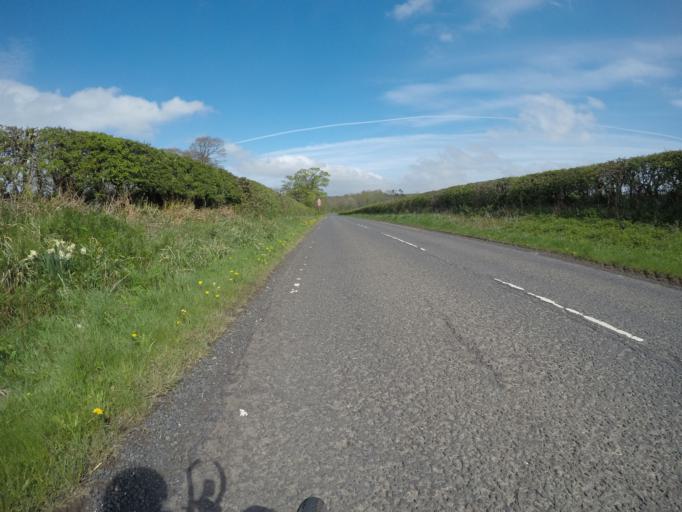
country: GB
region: Scotland
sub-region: East Ayrshire
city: Stewarton
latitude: 55.6694
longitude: -4.5316
